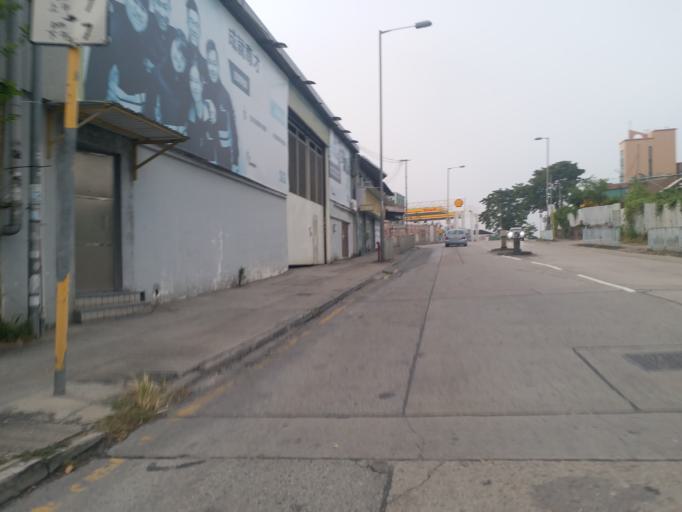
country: HK
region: Yuen Long
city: Yuen Long Kau Hui
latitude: 22.4387
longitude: 114.0112
